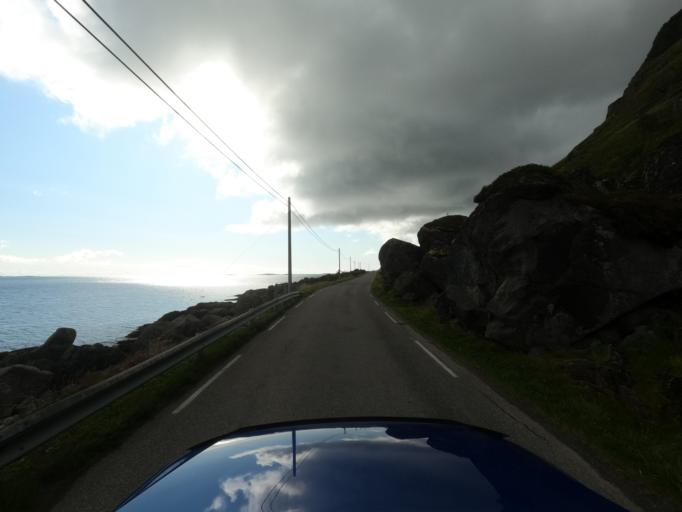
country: NO
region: Nordland
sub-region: Vestvagoy
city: Evjen
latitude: 68.1858
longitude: 13.9292
